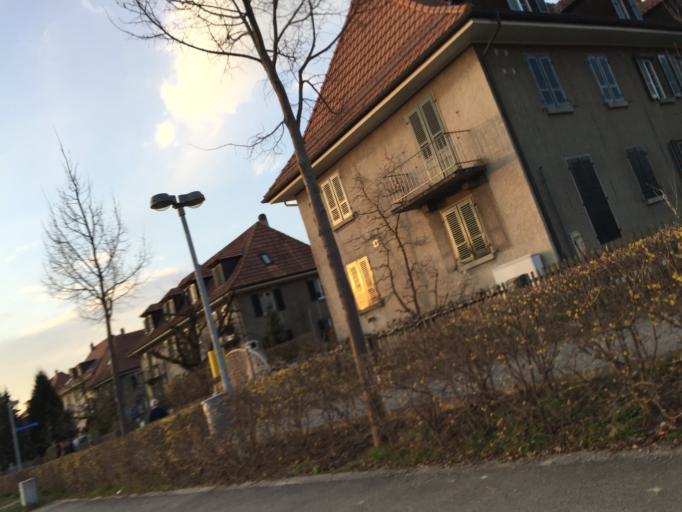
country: CH
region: Bern
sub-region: Bern-Mittelland District
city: Koniz
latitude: 46.9376
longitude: 7.4204
